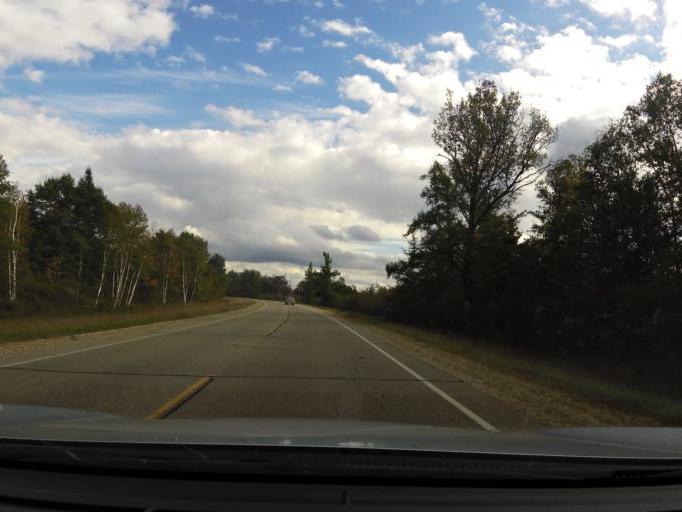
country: US
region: Michigan
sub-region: Roscommon County
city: Roscommon
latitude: 44.4351
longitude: -84.5106
